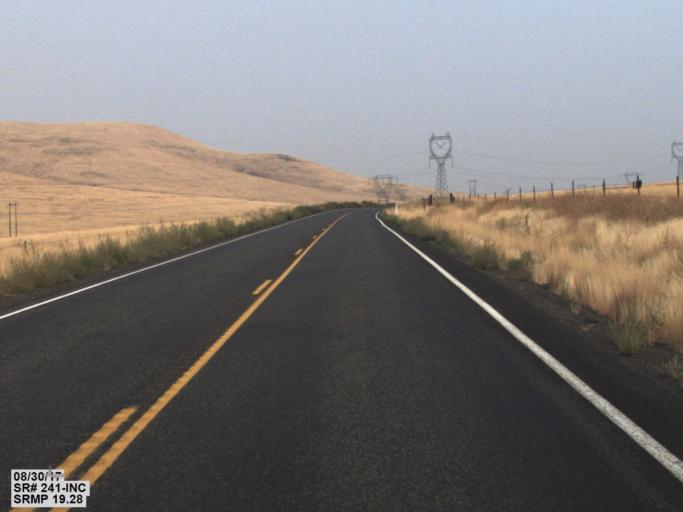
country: US
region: Washington
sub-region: Yakima County
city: Sunnyside
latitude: 46.4682
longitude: -119.9335
